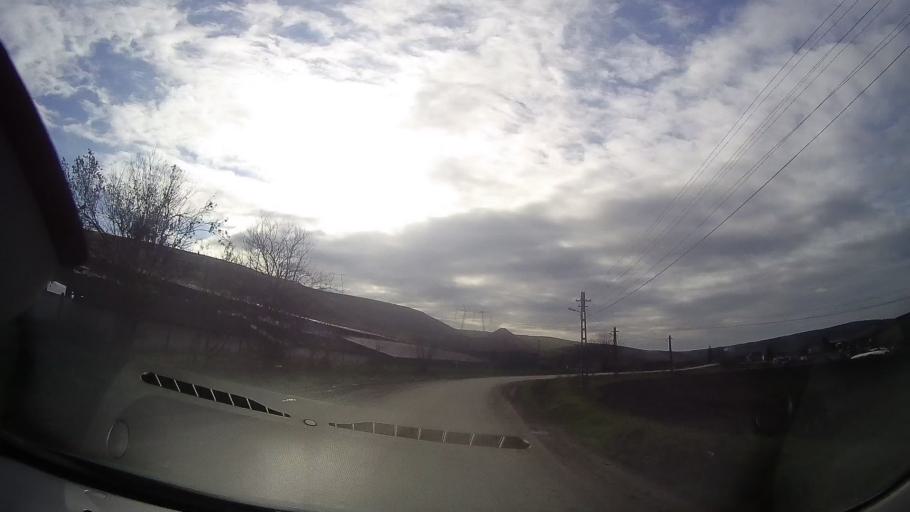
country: RO
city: Barza
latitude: 46.5493
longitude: 24.1290
